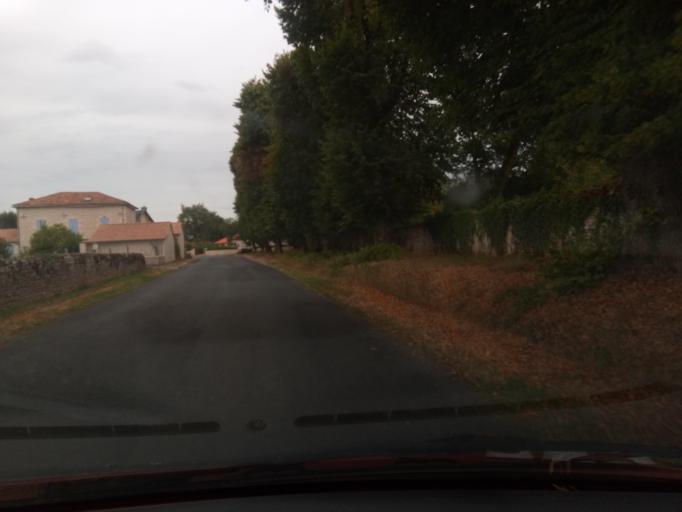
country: FR
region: Poitou-Charentes
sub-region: Departement de la Vienne
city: Saint-Savin
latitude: 46.5805
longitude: 0.7762
